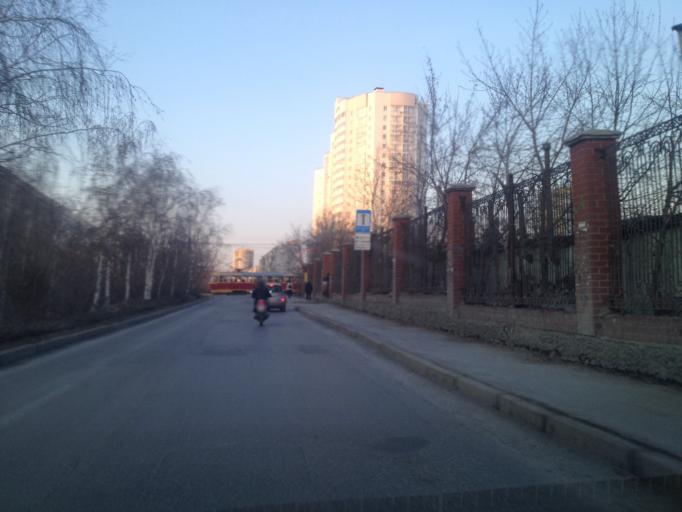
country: RU
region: Sverdlovsk
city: Sovkhoznyy
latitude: 56.8131
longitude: 60.5505
